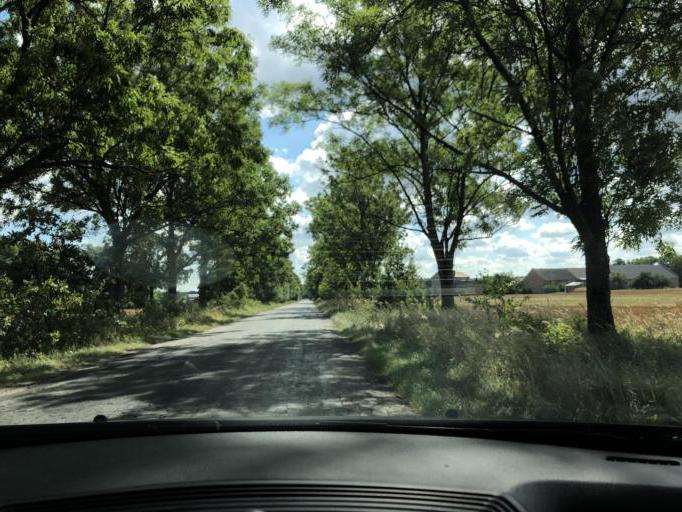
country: PL
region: Lodz Voivodeship
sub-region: Powiat wieruszowski
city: Czastary
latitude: 51.2325
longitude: 18.3523
